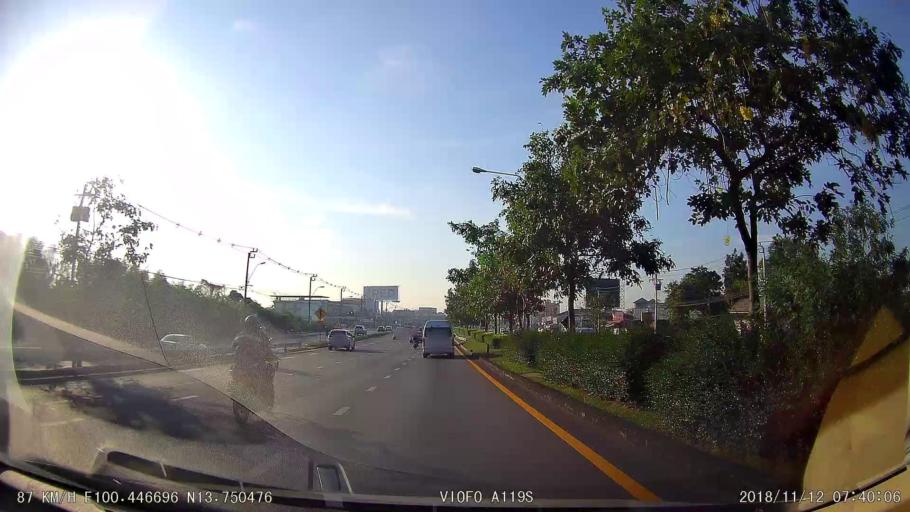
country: TH
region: Bangkok
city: Taling Chan
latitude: 13.7493
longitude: 100.4471
